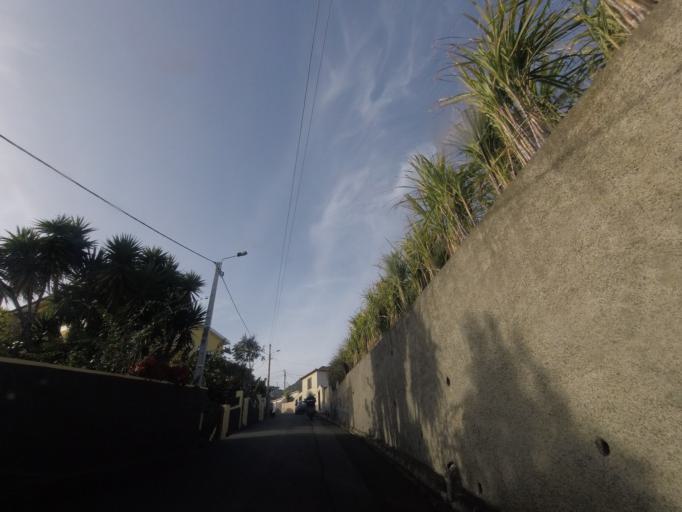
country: PT
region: Madeira
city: Camara de Lobos
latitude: 32.6531
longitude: -16.9863
